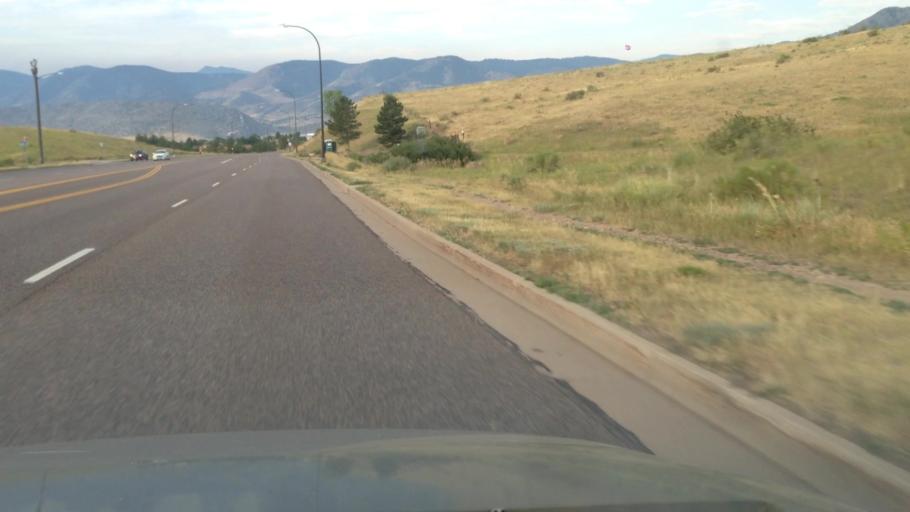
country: US
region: Colorado
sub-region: Jefferson County
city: West Pleasant View
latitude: 39.6878
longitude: -105.1538
